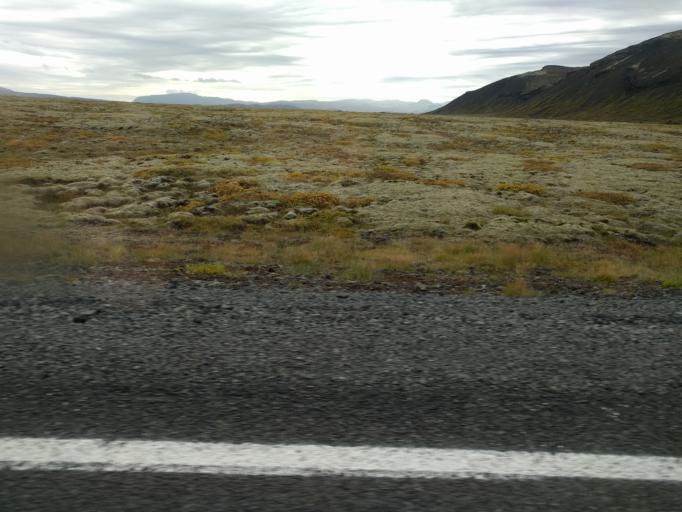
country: IS
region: South
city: Hveragerdi
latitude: 64.1952
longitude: -21.0199
